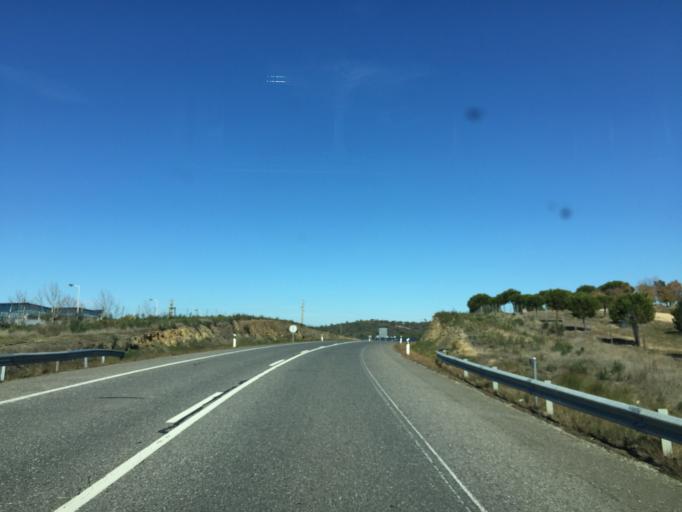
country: PT
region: Castelo Branco
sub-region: Castelo Branco
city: Castelo Branco
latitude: 39.8194
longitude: -7.5184
